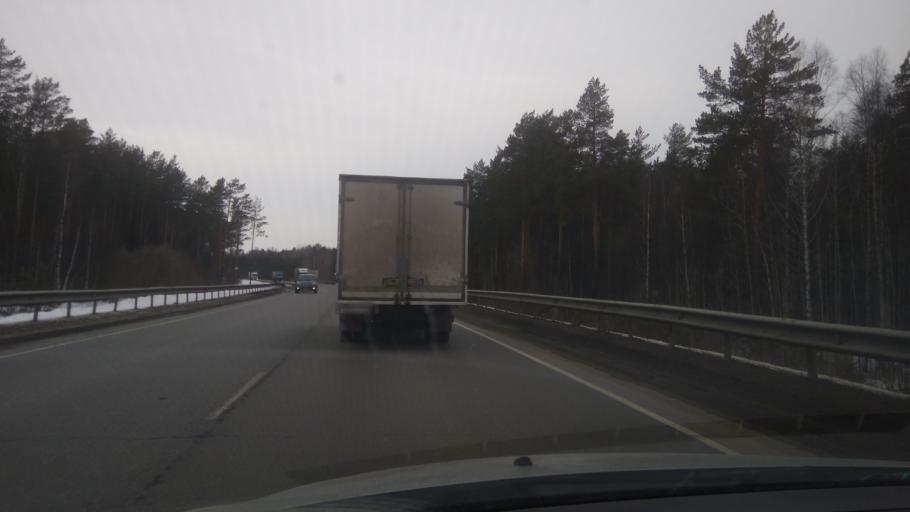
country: RU
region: Sverdlovsk
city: Ufimskiy
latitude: 56.7676
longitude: 58.1790
